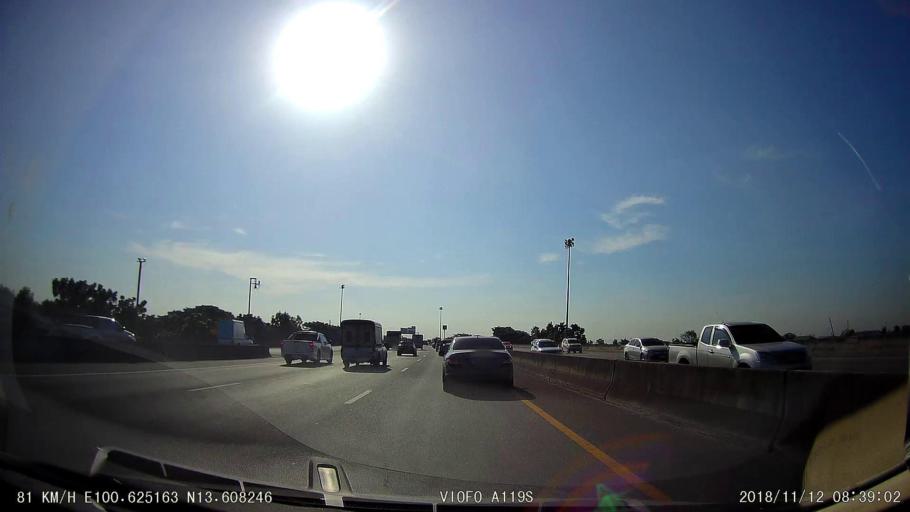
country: TH
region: Samut Prakan
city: Samut Prakan
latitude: 13.6080
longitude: 100.6254
